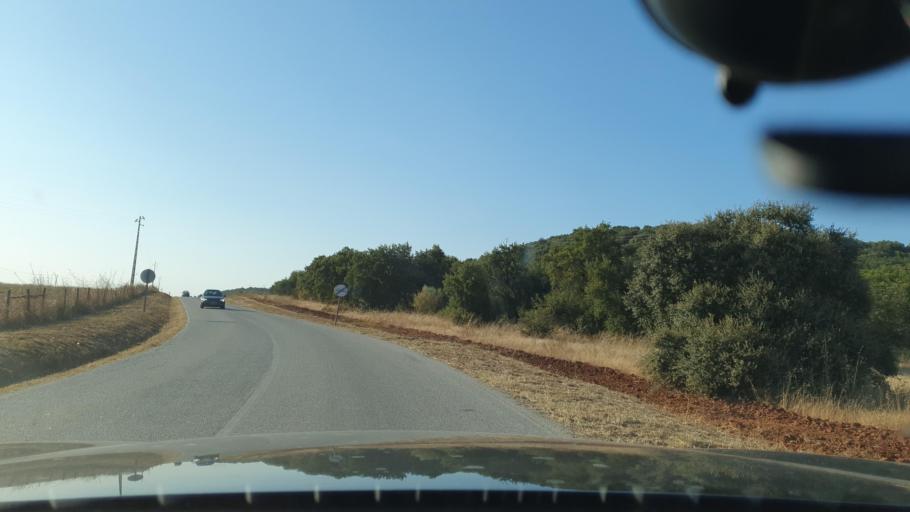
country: PT
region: Evora
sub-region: Estremoz
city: Estremoz
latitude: 38.8842
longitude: -7.6461
